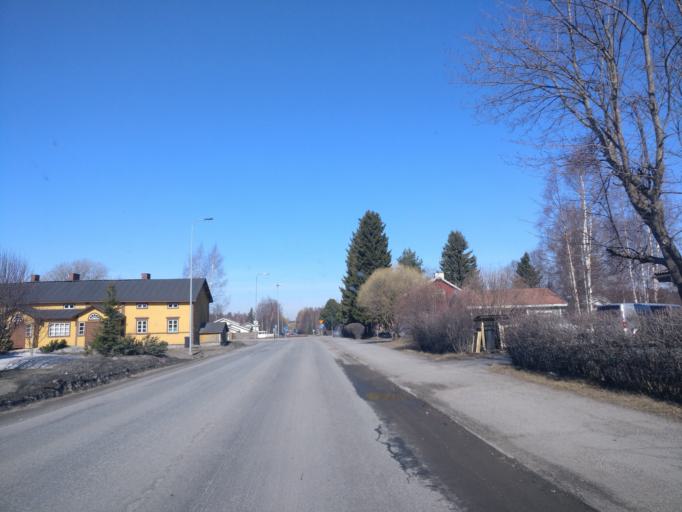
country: FI
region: Lapland
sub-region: Kemi-Tornio
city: Kemi
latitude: 65.7328
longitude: 24.5970
